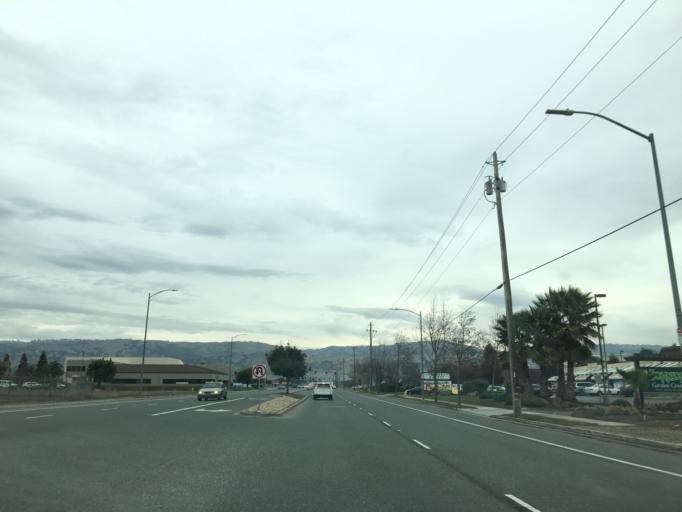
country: US
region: California
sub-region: Santa Clara County
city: Morgan Hill
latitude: 37.1159
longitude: -121.6351
